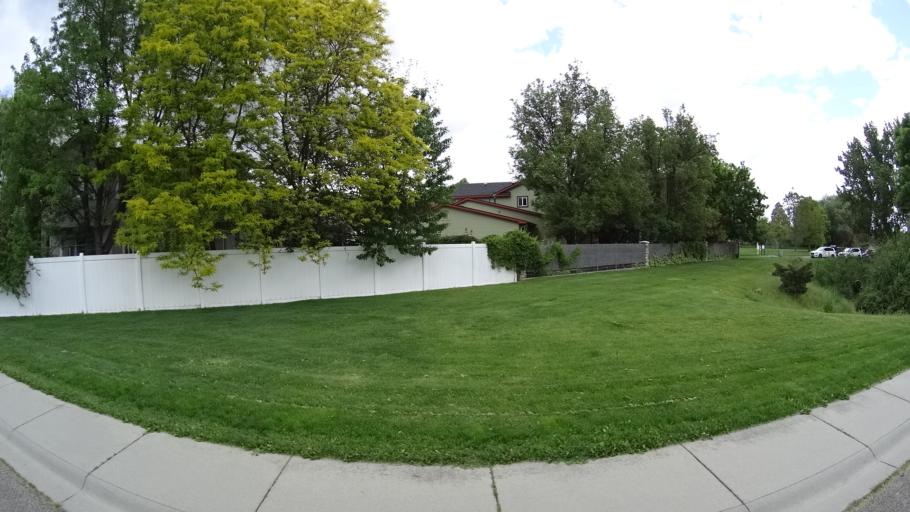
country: US
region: Idaho
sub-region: Ada County
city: Garden City
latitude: 43.6689
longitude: -116.2634
